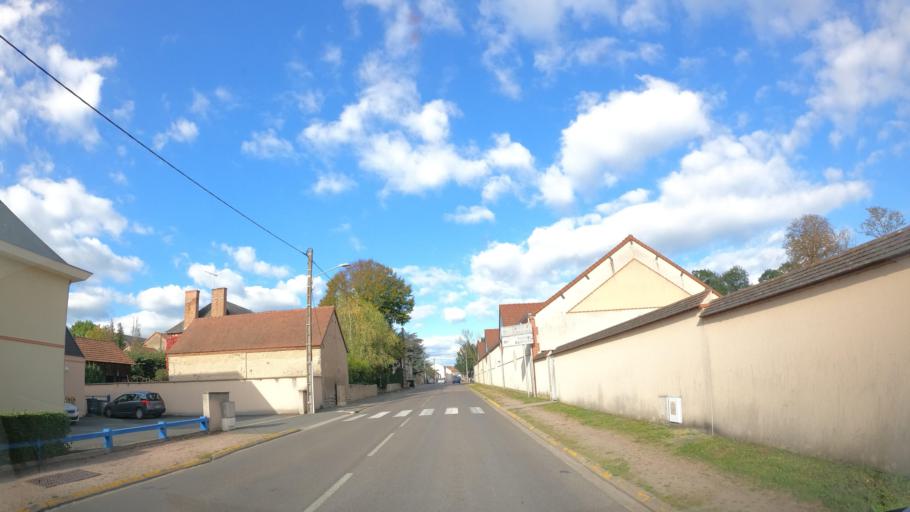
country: FR
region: Auvergne
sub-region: Departement de l'Allier
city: Dompierre-sur-Besbre
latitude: 46.5184
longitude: 3.6794
